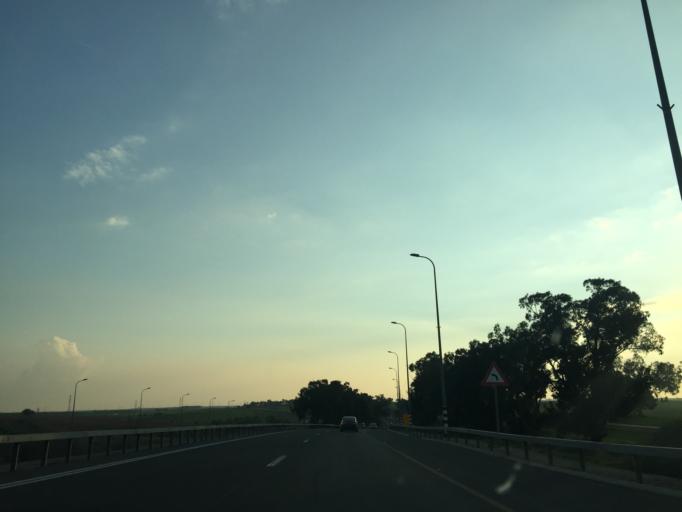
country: IL
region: Southern District
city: Qiryat Gat
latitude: 31.4904
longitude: 34.7790
